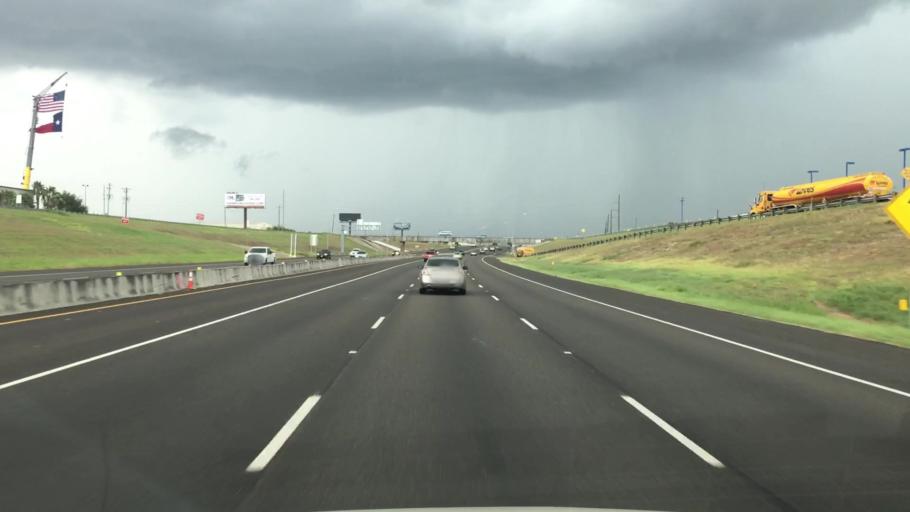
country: US
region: Texas
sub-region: Nueces County
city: Corpus Christi
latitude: 27.8053
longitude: -97.4855
